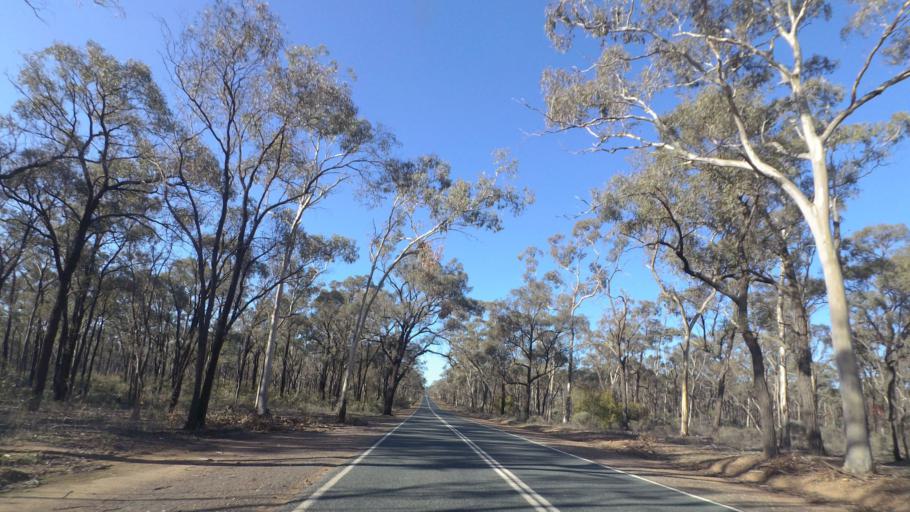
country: AU
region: Victoria
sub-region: Greater Bendigo
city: Epsom
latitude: -36.6688
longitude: 144.4247
